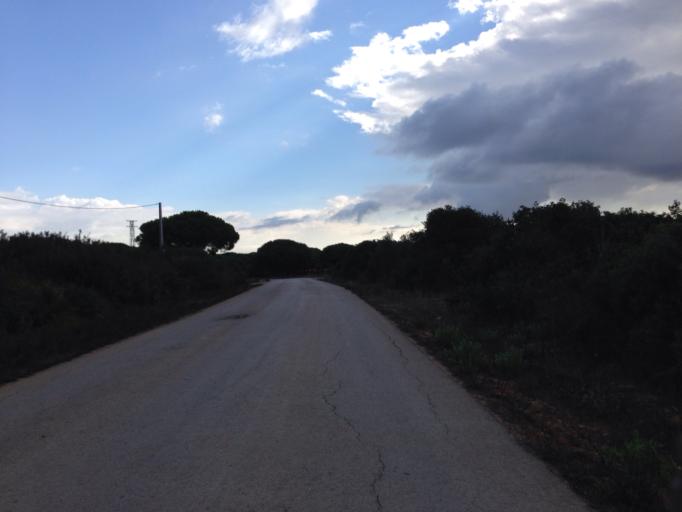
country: ES
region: Andalusia
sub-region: Provincia de Cadiz
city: Conil de la Frontera
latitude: 36.3093
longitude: -6.1176
